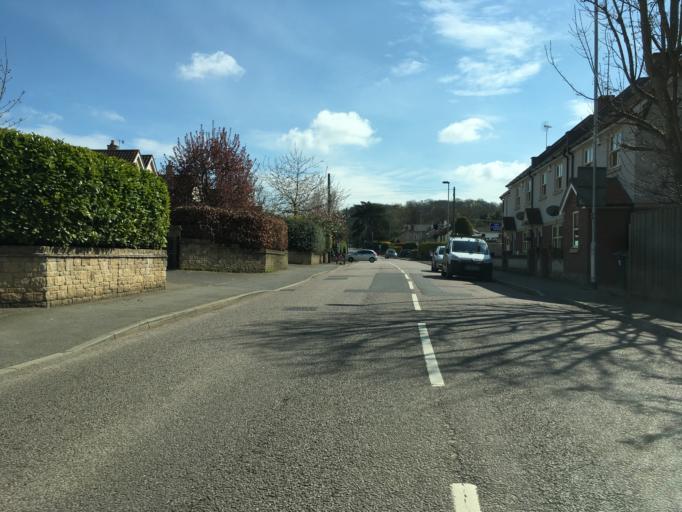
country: GB
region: England
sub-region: South Gloucestershire
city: Almondsbury
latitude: 51.5385
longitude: -2.6170
